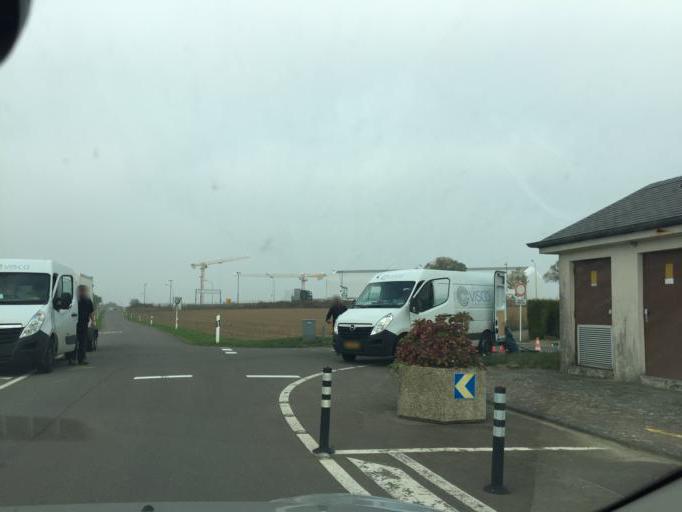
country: LU
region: Luxembourg
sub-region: Canton de Luxembourg
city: Sandweiler
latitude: 49.6132
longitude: 6.2070
